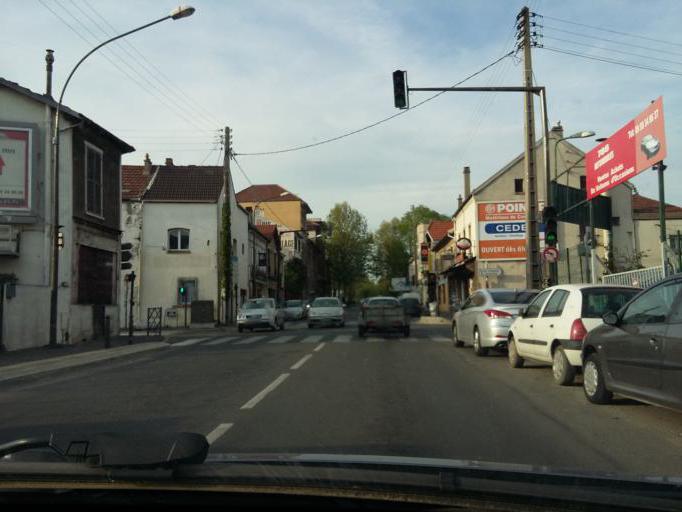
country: FR
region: Ile-de-France
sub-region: Departement du Val-d'Oise
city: Sannois
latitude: 48.9584
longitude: 2.2572
